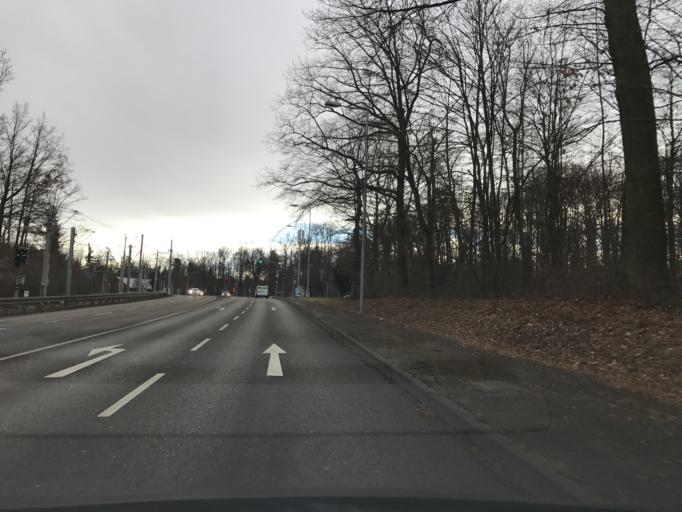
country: DE
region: Baden-Wuerttemberg
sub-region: Regierungsbezirk Stuttgart
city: Stuttgart
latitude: 48.7550
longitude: 9.1936
